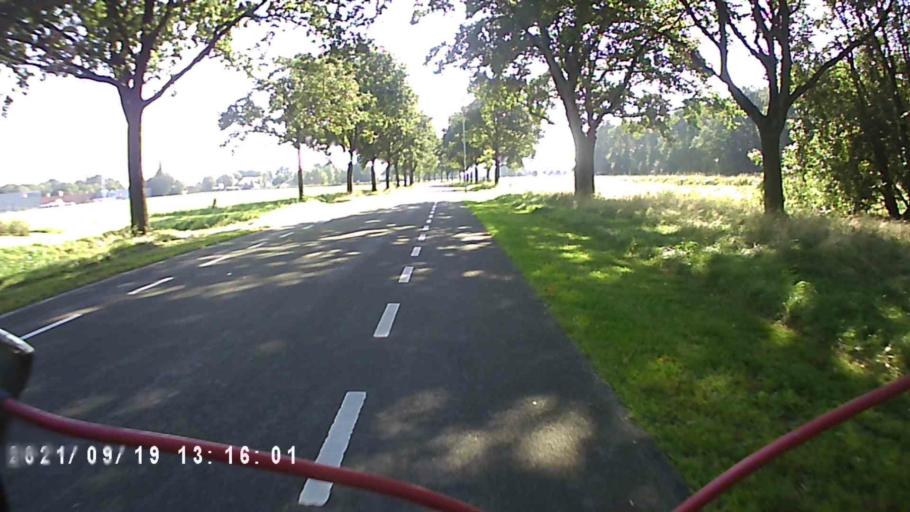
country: NL
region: Groningen
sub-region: Gemeente  Oldambt
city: Winschoten
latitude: 53.1572
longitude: 6.9939
